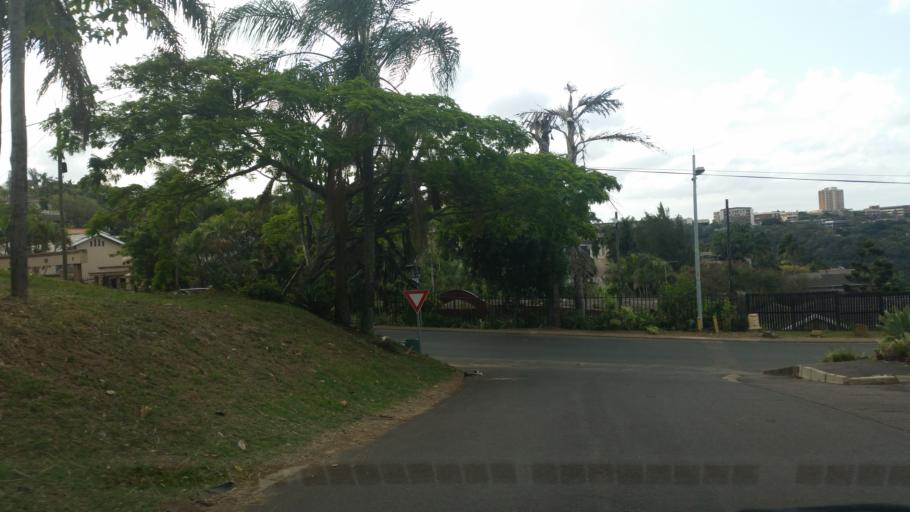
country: ZA
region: KwaZulu-Natal
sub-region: eThekwini Metropolitan Municipality
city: Berea
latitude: -29.8279
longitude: 30.9427
